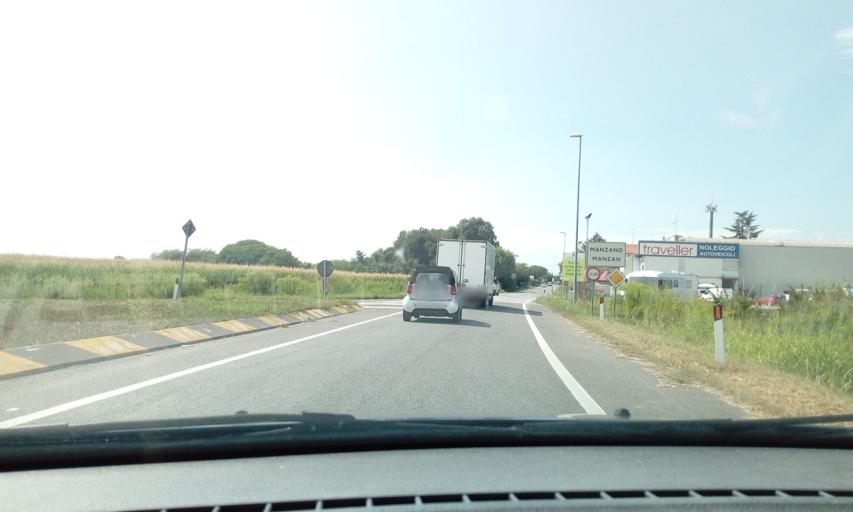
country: IT
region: Friuli Venezia Giulia
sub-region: Provincia di Udine
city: Manzano
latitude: 45.9824
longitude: 13.3800
